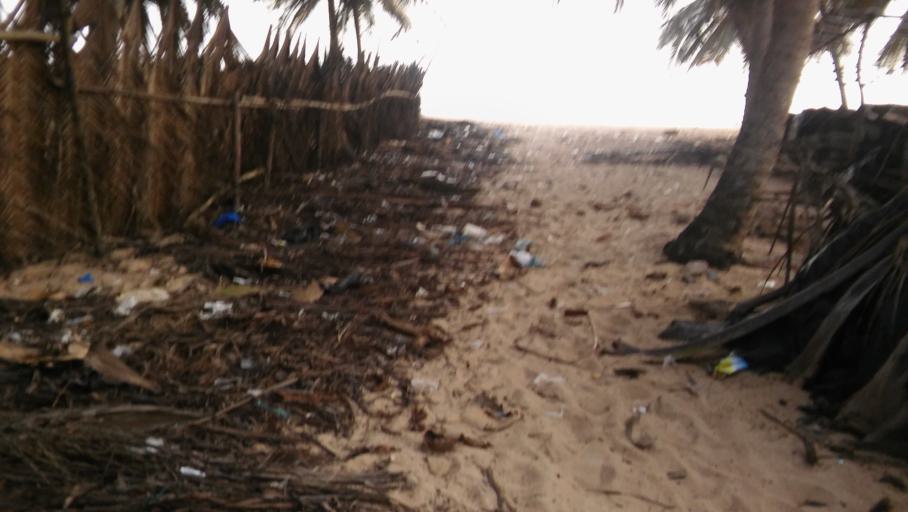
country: CI
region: Sud-Comoe
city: Grand-Bassam
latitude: 5.1924
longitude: -3.7245
